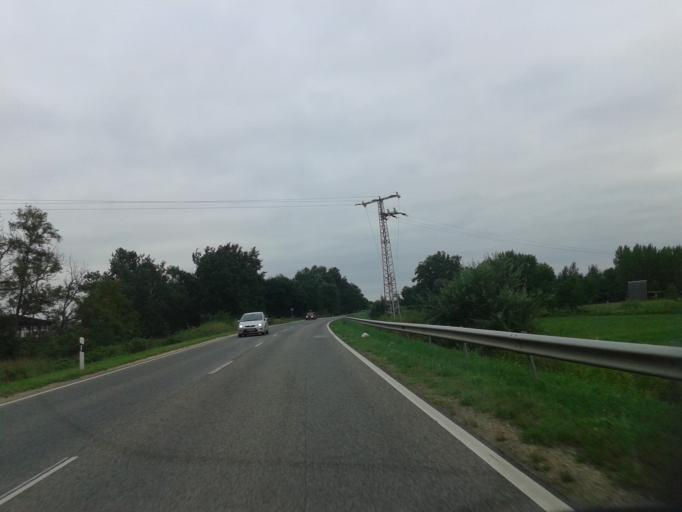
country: HU
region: Pest
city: Domsod
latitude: 47.1078
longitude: 19.0122
